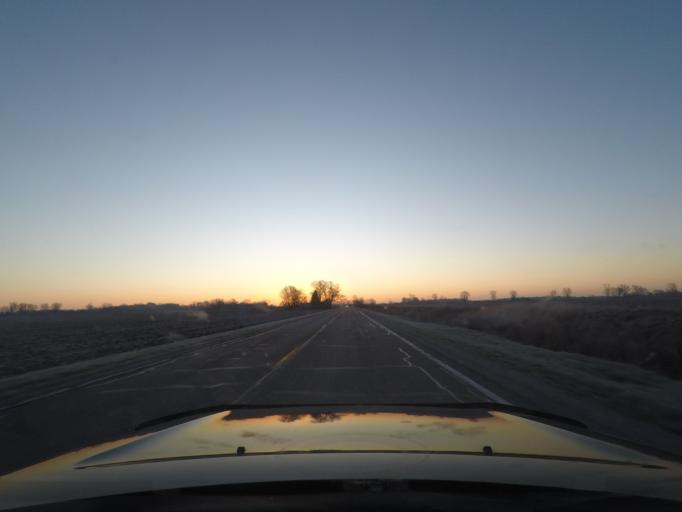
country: US
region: Indiana
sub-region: LaPorte County
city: Kingsford Heights
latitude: 41.4775
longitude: -86.6152
